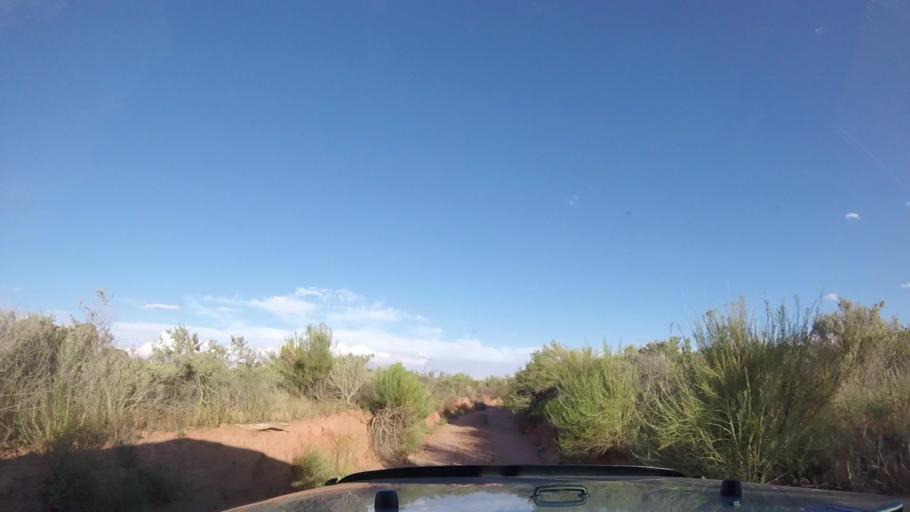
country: US
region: Utah
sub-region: Grand County
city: Moab
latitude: 38.1917
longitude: -109.7799
